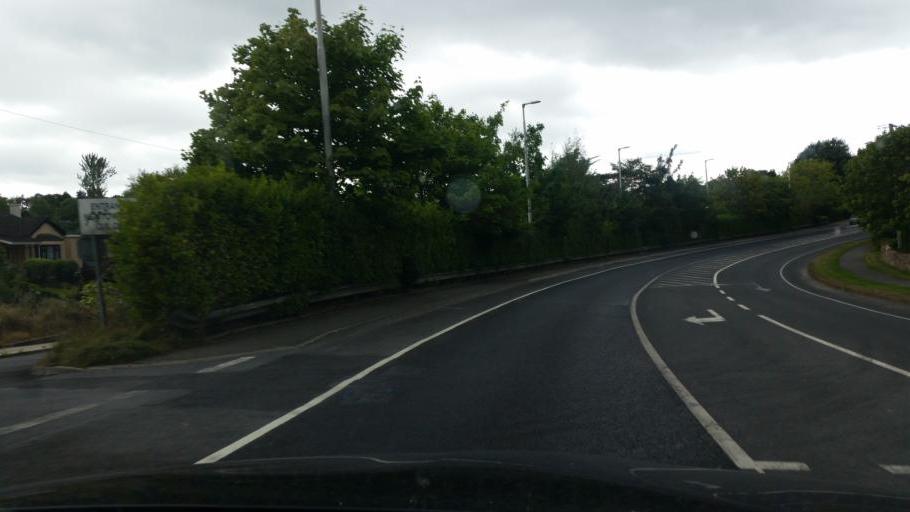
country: IE
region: Leinster
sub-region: Loch Garman
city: Loch Garman
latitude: 52.3408
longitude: -6.4797
